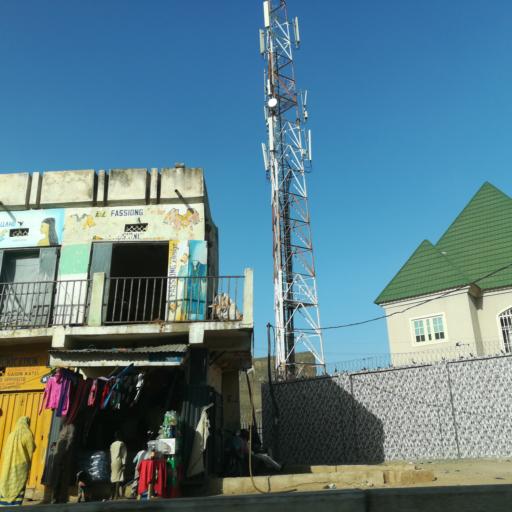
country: NG
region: Kano
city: Kano
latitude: 12.0138
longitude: 8.4989
